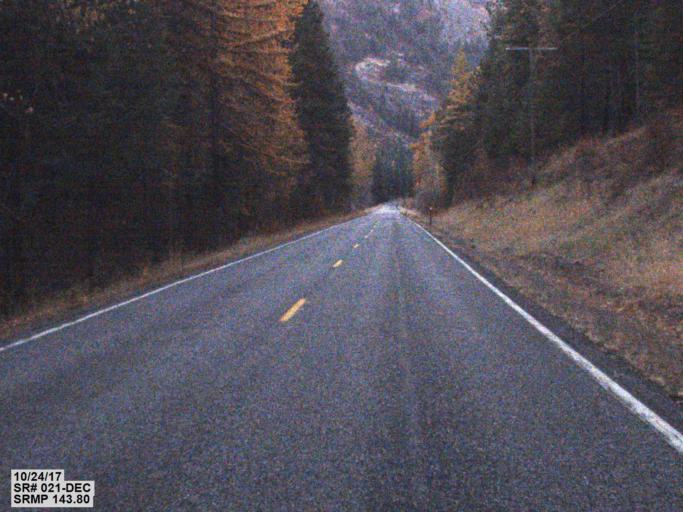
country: US
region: Washington
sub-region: Ferry County
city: Republic
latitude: 48.4347
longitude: -118.7349
